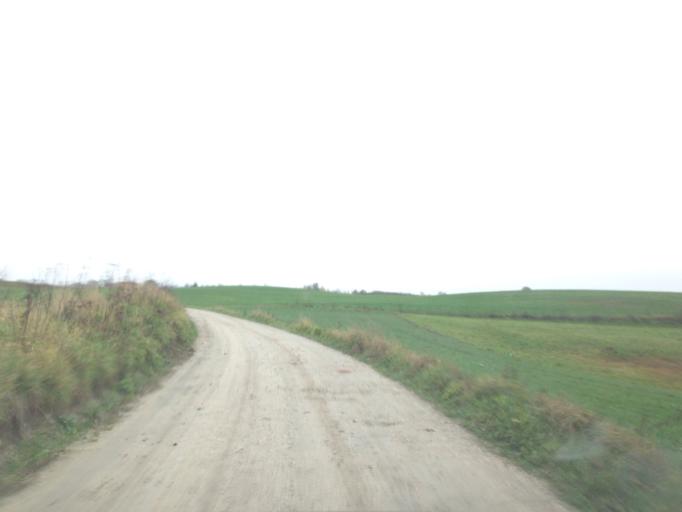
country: PL
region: Kujawsko-Pomorskie
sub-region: Powiat brodnicki
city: Bartniczka
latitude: 53.2197
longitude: 19.6013
